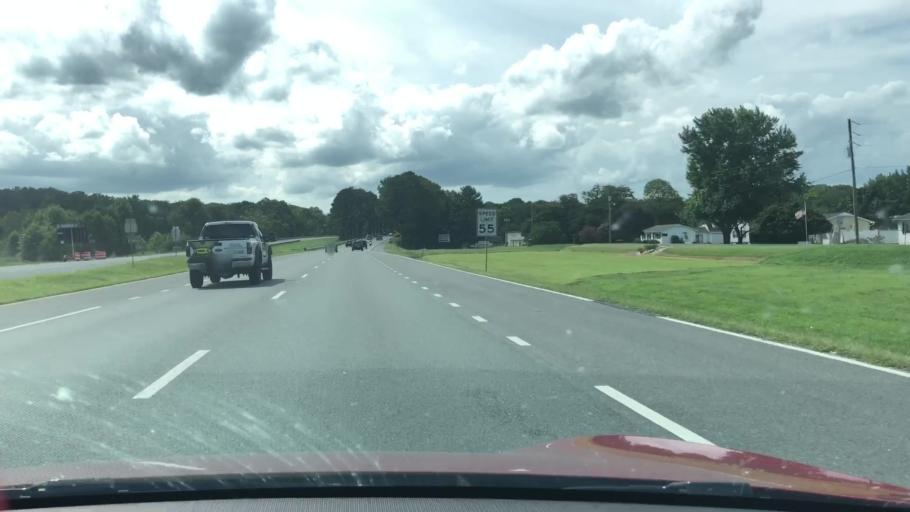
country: US
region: Maryland
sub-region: Worcester County
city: Pocomoke City
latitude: 38.0791
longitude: -75.5776
